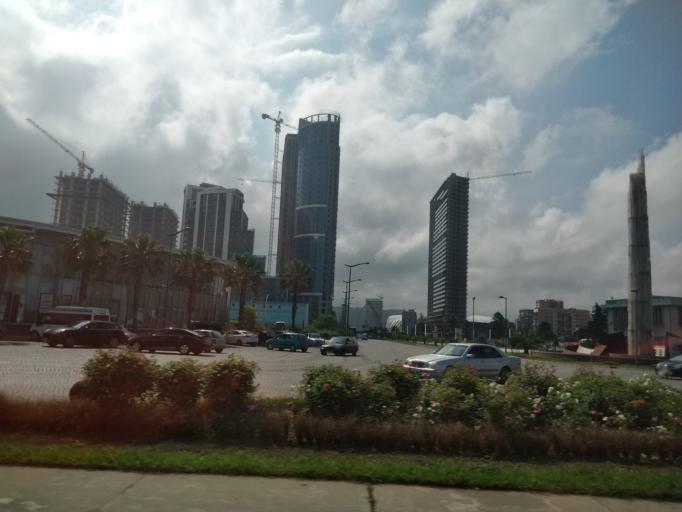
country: GE
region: Ajaria
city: Batumi
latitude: 41.6411
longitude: 41.6144
